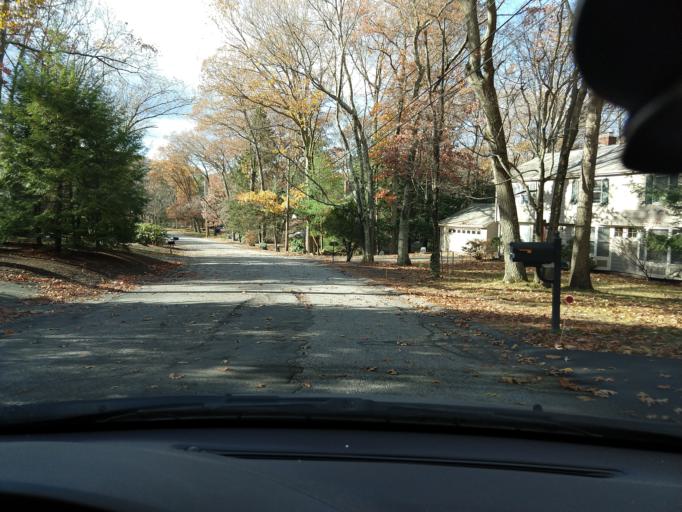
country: US
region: Massachusetts
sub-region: Middlesex County
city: Bedford
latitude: 42.4868
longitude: -71.2425
